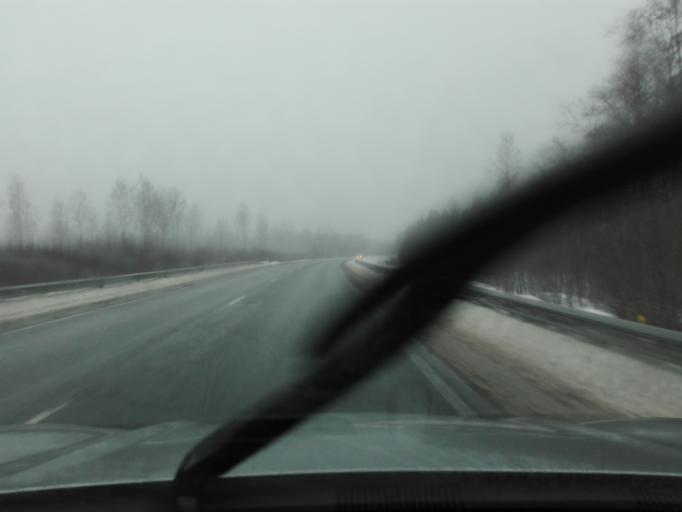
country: EE
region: Raplamaa
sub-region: Kohila vald
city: Kohila
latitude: 59.1375
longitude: 24.7916
